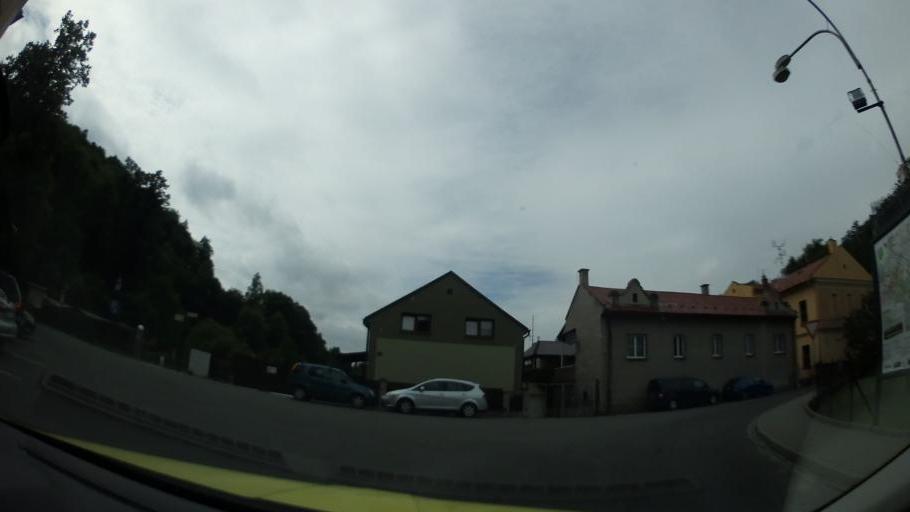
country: CZ
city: Stramberk
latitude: 49.5873
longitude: 18.1222
